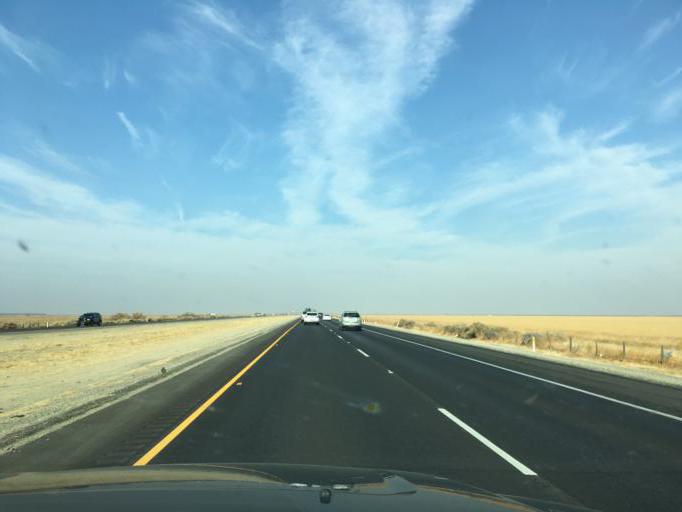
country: US
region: California
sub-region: Kern County
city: Lost Hills
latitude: 35.6488
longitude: -119.6773
